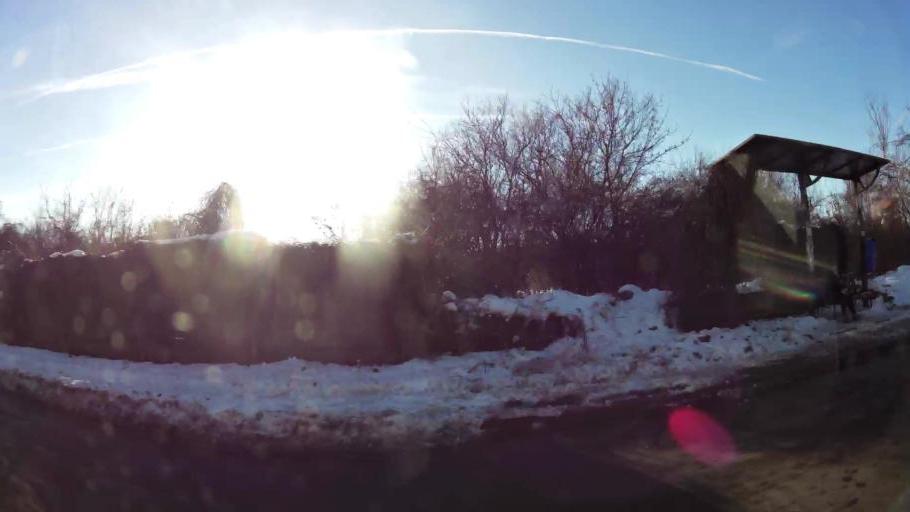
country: RO
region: Ilfov
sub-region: Comuna Fundeni-Dobroesti
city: Fundeni
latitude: 44.4766
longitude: 26.1440
